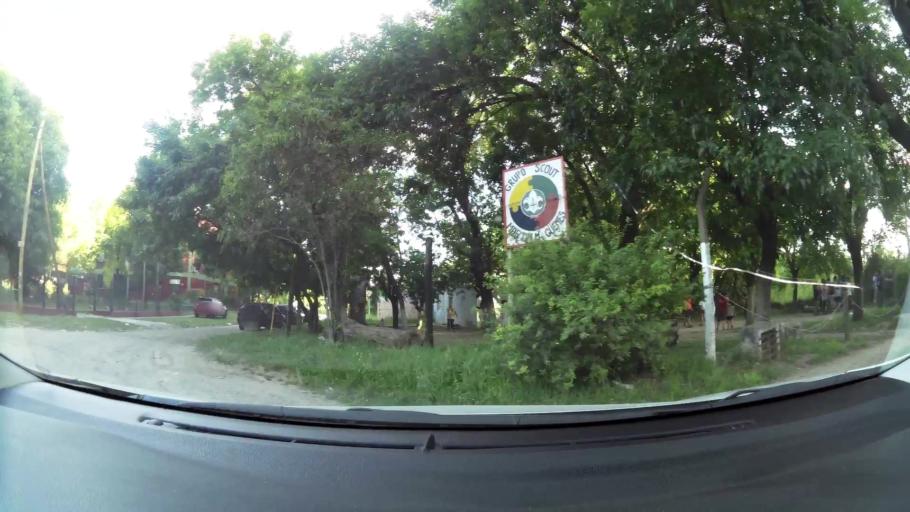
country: AR
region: Buenos Aires F.D.
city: Villa Lugano
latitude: -34.6995
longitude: -58.4926
